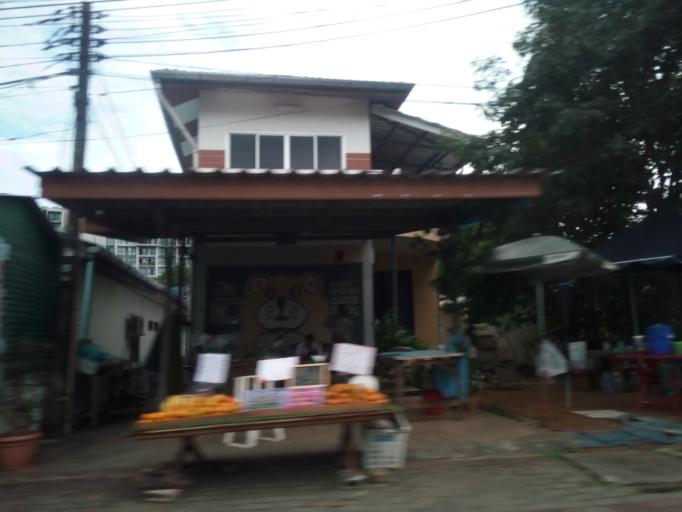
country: TH
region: Phuket
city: Ban Talat Nua
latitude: 7.8798
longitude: 98.3788
